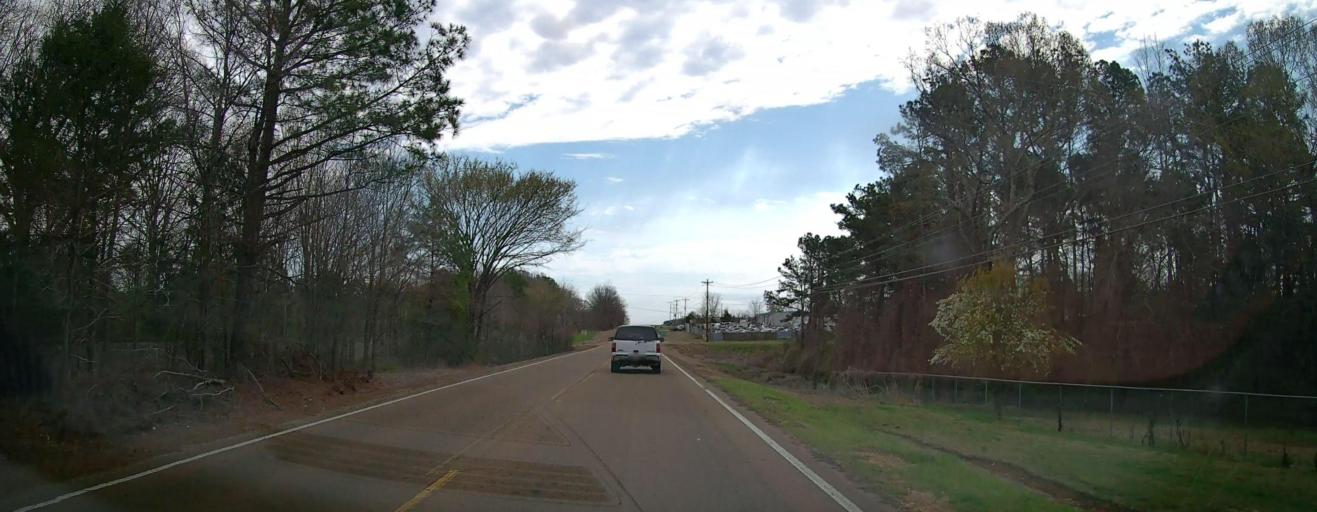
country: US
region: Mississippi
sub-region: Marshall County
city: Byhalia
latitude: 34.8867
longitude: -89.7252
